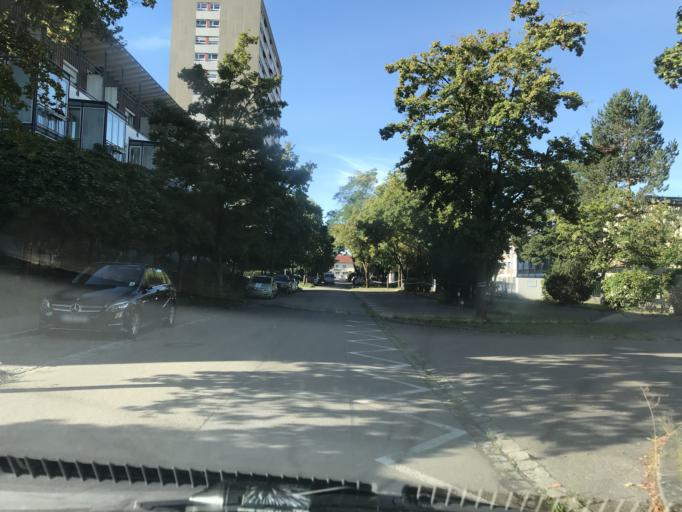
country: DE
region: Baden-Wuerttemberg
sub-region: Freiburg Region
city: Loerrach
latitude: 47.6211
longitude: 7.6624
